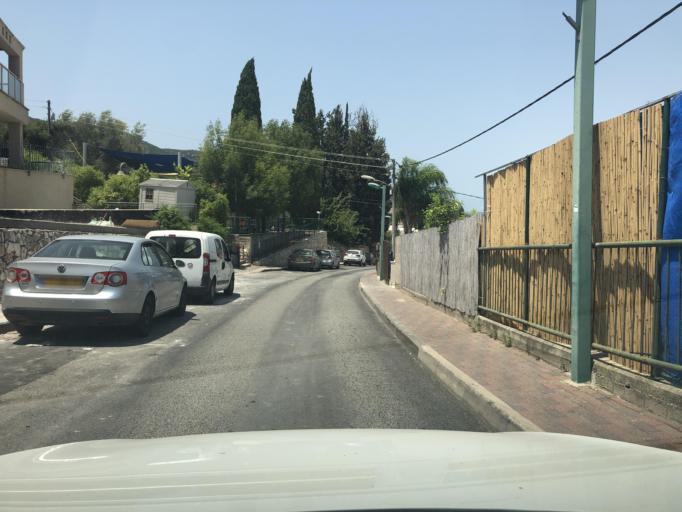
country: IL
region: Haifa
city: Daliyat el Karmil
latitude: 32.6606
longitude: 35.1103
